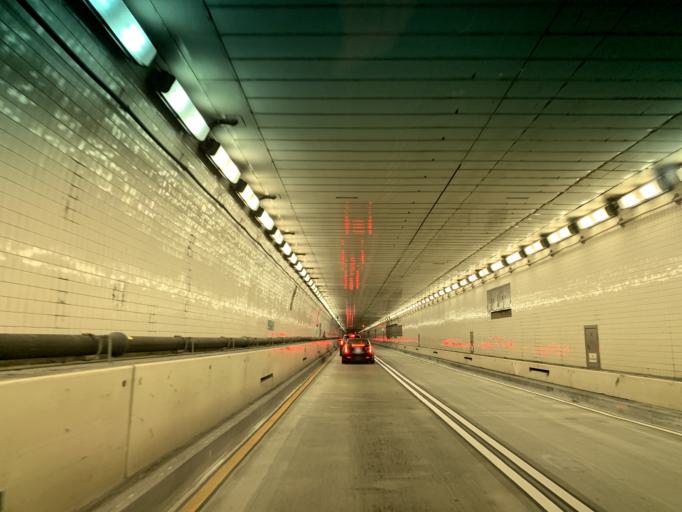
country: US
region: Maryland
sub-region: Anne Arundel County
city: Brooklyn Park
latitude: 39.2467
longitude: -76.5762
